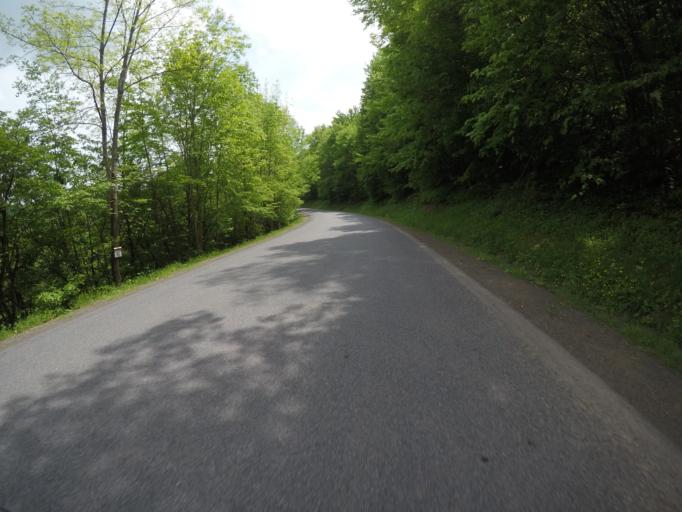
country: US
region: New York
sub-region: Delaware County
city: Stamford
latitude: 42.2289
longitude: -74.6922
